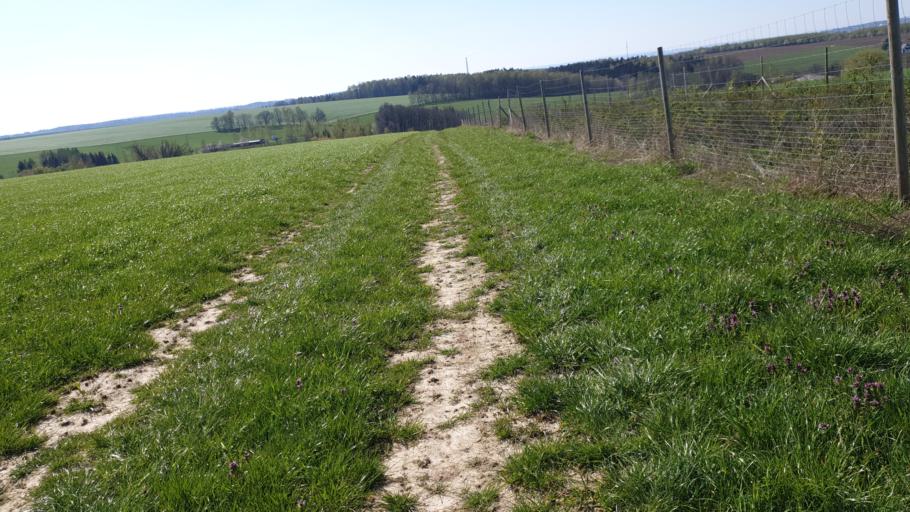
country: DE
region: Saxony
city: Claussnitz
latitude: 50.9213
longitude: 12.9119
